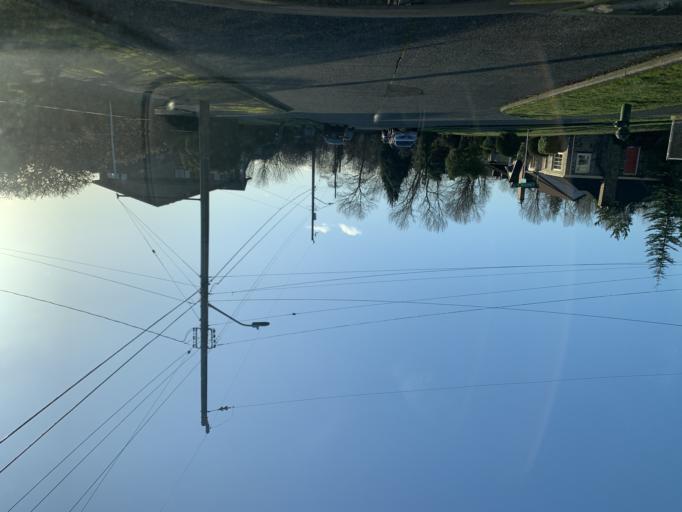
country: US
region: Washington
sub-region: King County
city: Seattle
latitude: 47.5763
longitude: -122.3174
